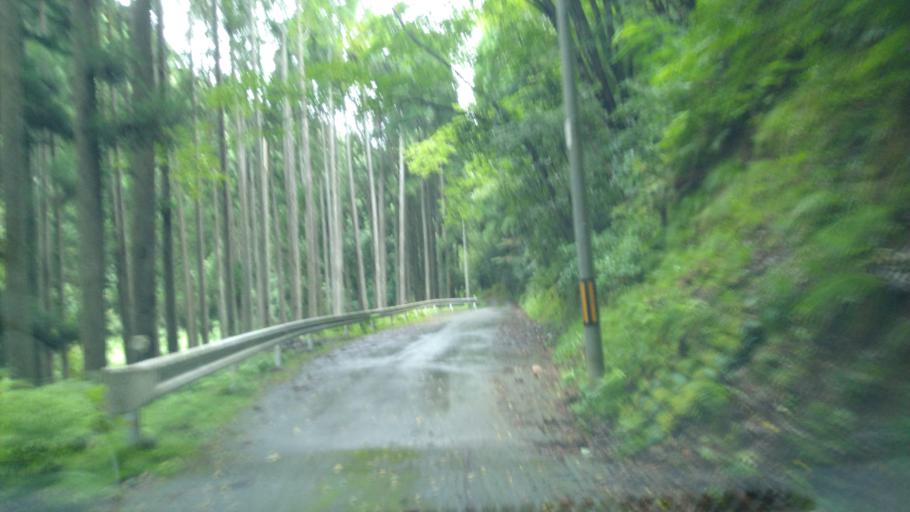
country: JP
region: Kyoto
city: Ayabe
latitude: 35.2296
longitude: 135.2709
